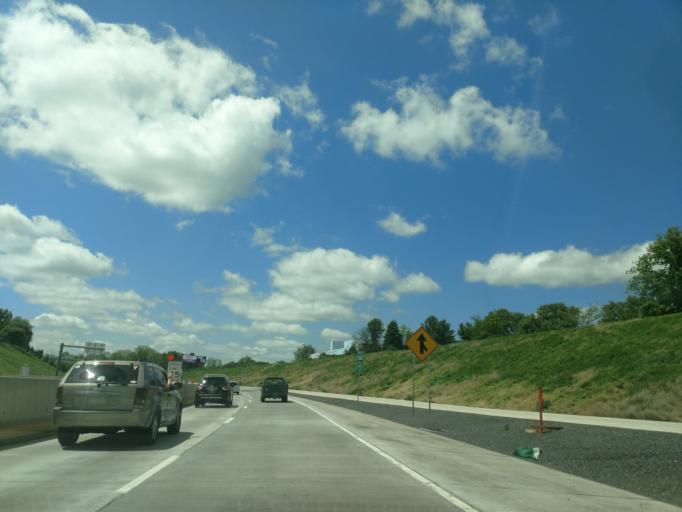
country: US
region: Pennsylvania
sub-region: Montgomery County
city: Audubon
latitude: 40.1146
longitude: -75.4215
